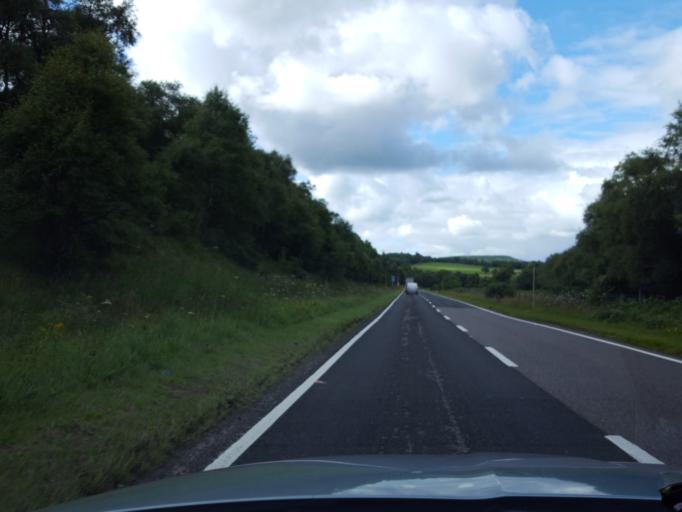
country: GB
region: Scotland
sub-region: Highland
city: Grantown on Spey
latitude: 57.3232
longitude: -3.5569
